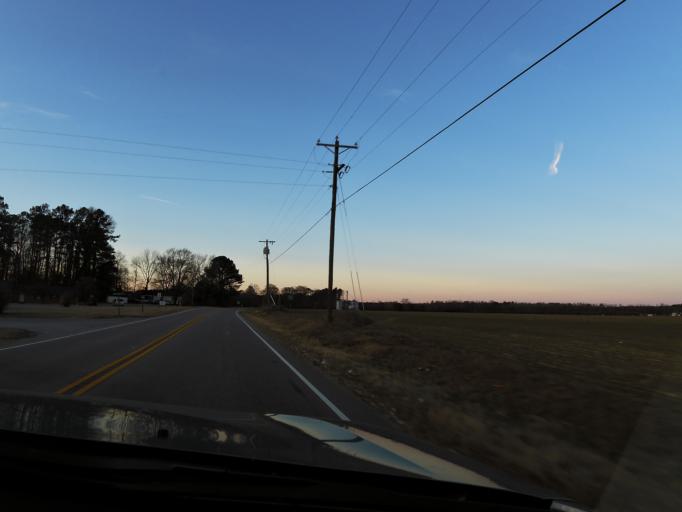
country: US
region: Virginia
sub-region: Southampton County
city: Courtland
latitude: 36.7281
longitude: -77.0724
